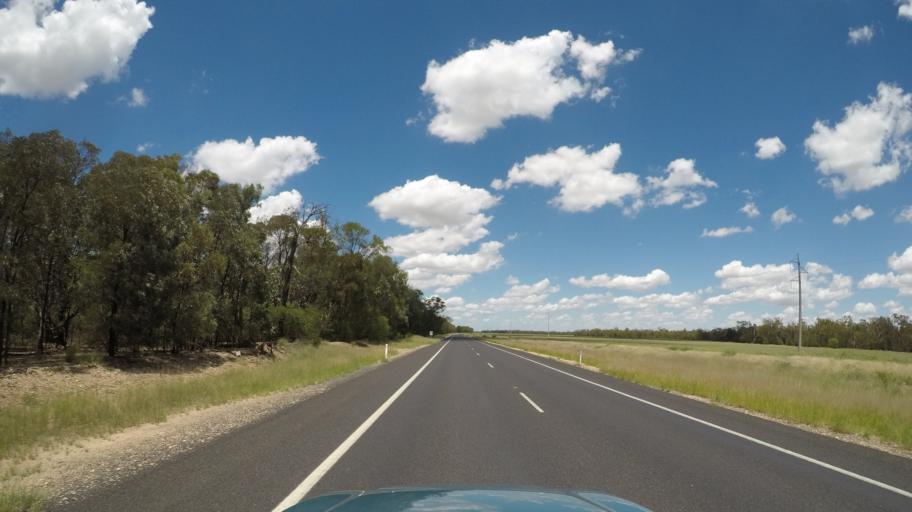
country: AU
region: Queensland
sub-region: Goondiwindi
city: Goondiwindi
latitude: -28.1112
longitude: 150.7177
